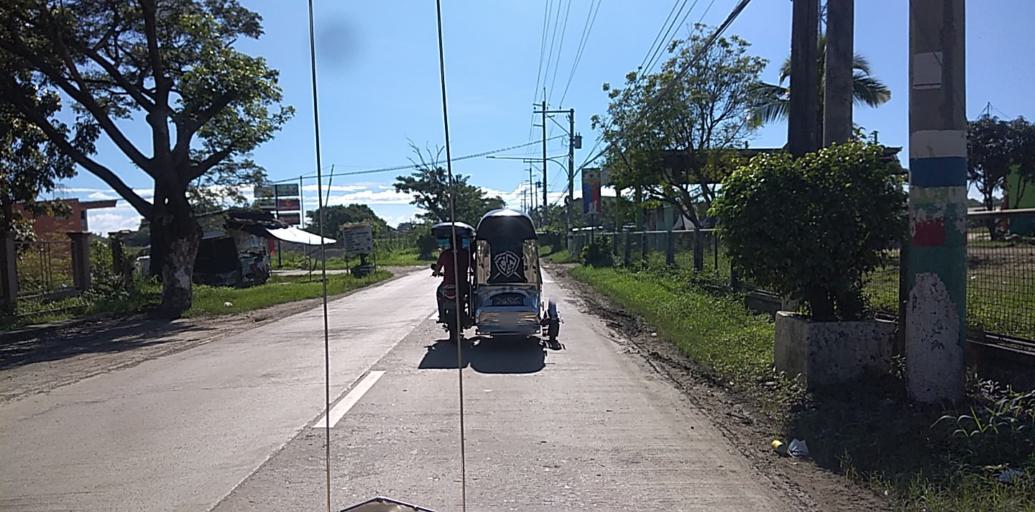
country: PH
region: Central Luzon
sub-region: Province of Pampanga
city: San Luis
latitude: 15.0476
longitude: 120.7852
